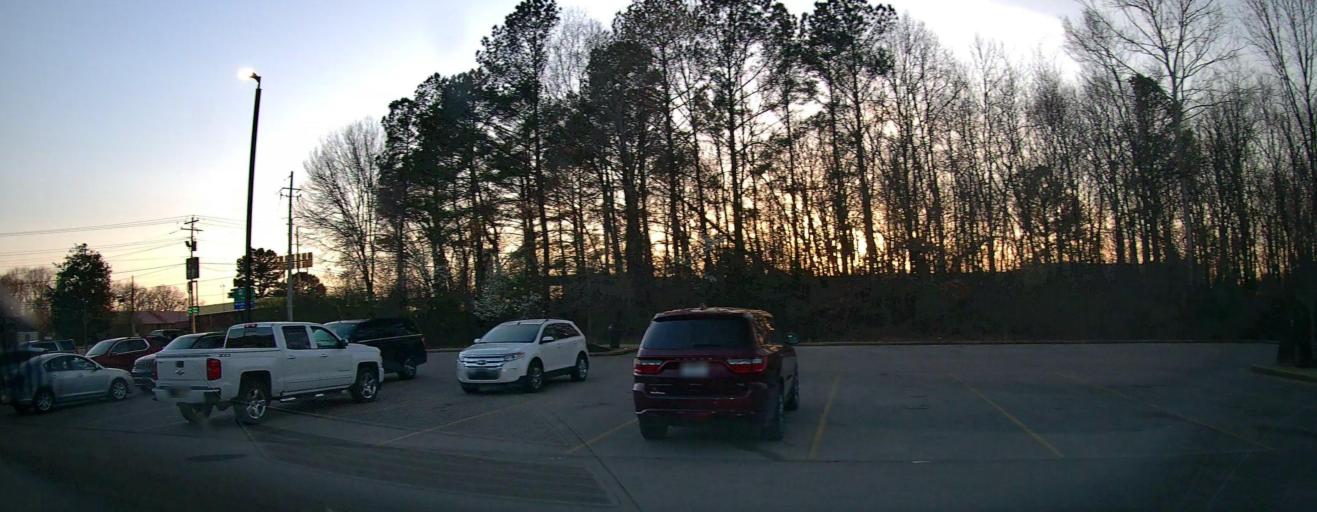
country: US
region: Mississippi
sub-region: Alcorn County
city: Corinth
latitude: 34.9317
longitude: -88.5431
